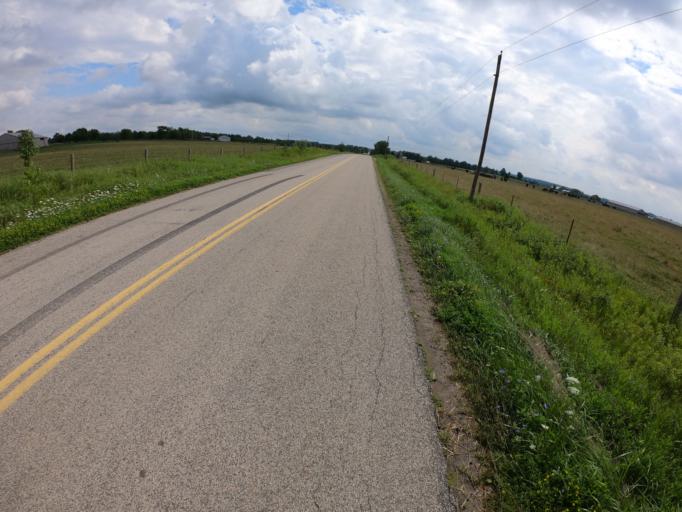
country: CA
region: Ontario
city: Waterloo
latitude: 43.4483
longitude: -80.7021
